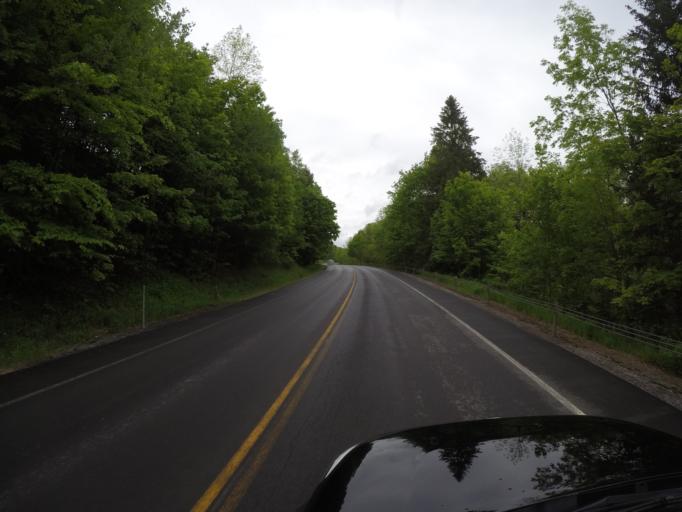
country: US
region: New York
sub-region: Delaware County
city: Delhi
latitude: 42.1939
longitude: -74.7887
